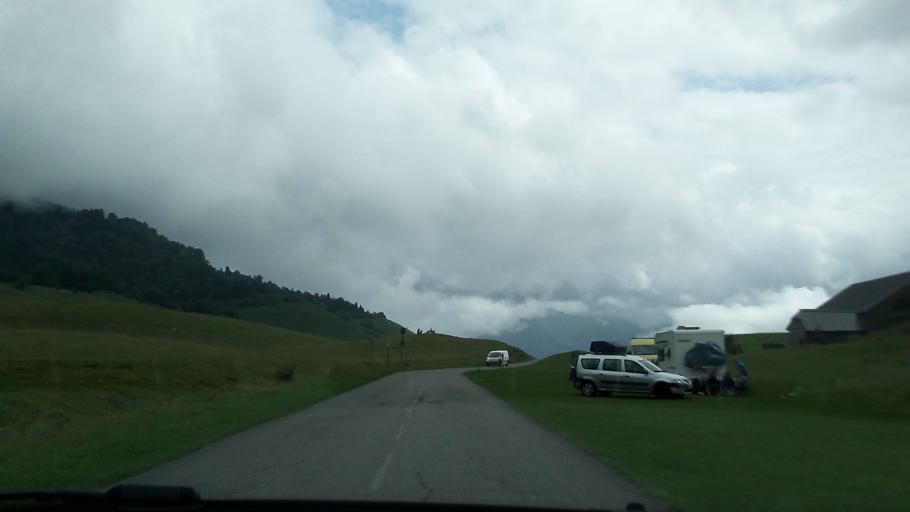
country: FR
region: Aquitaine
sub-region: Departement des Pyrenees-Atlantiques
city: Louvie-Juzon
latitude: 43.0655
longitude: -0.4667
